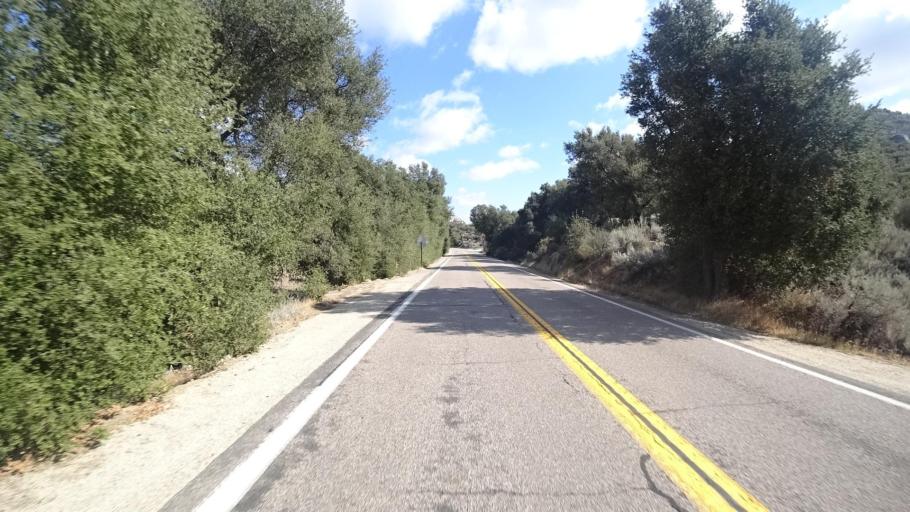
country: US
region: California
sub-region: San Diego County
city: Campo
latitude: 32.7142
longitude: -116.4974
